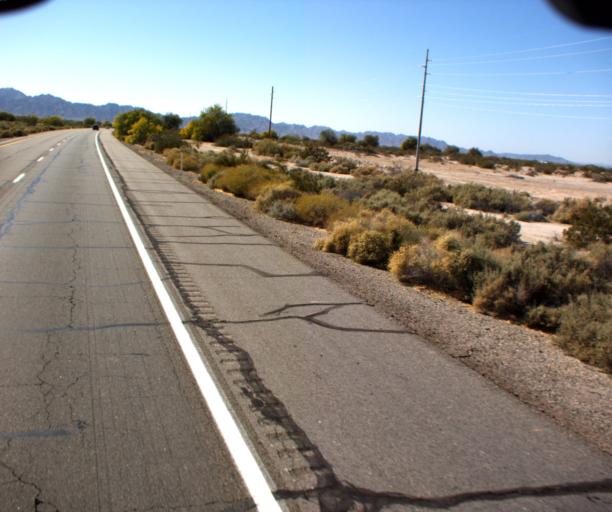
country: US
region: Arizona
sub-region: Yuma County
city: Wellton
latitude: 32.6488
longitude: -114.2023
